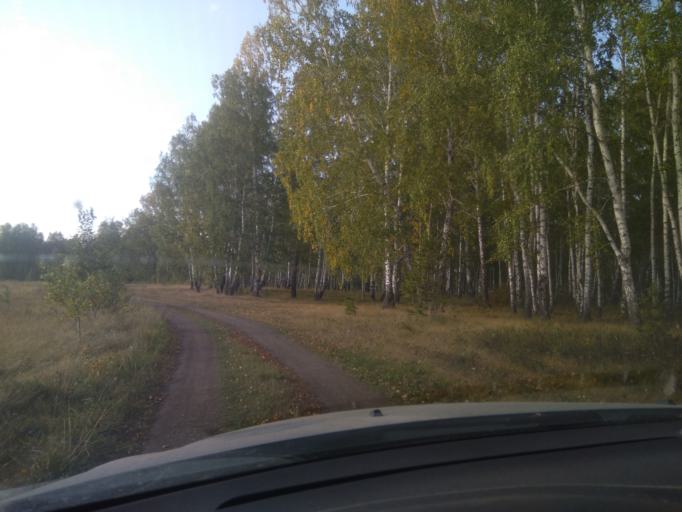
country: RU
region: Sverdlovsk
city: Pokrovskoye
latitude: 56.4296
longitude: 61.6088
